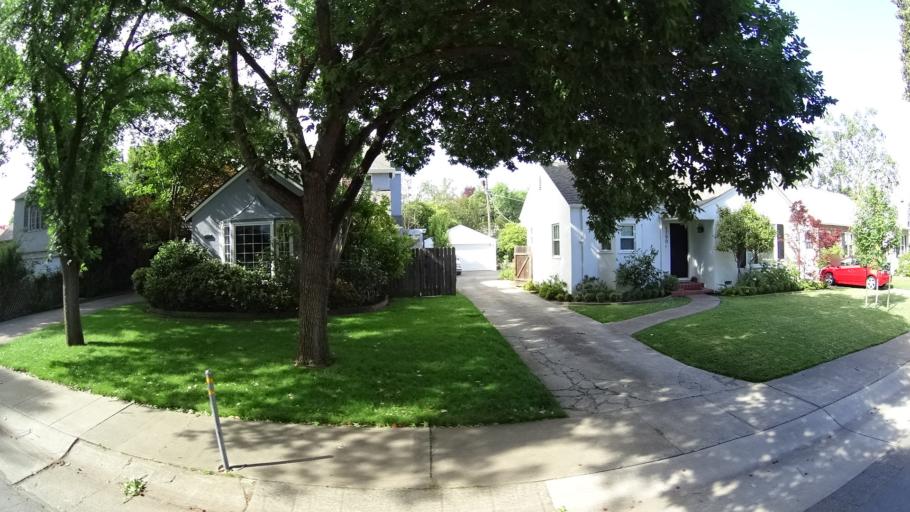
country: US
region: California
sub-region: Sacramento County
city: Sacramento
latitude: 38.5480
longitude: -121.4949
